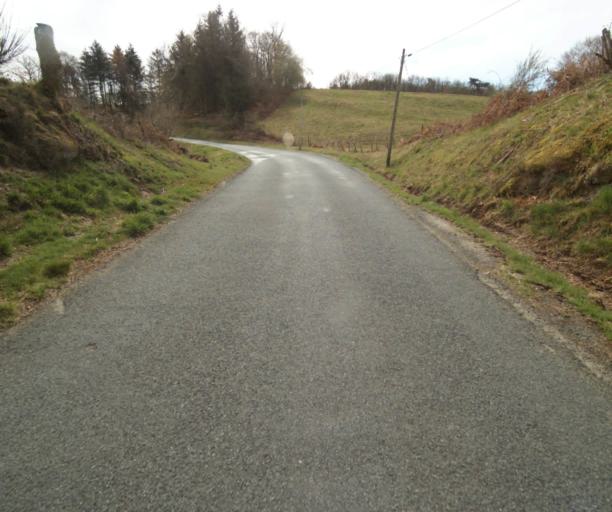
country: FR
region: Limousin
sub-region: Departement de la Correze
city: Correze
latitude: 45.3792
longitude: 1.8949
